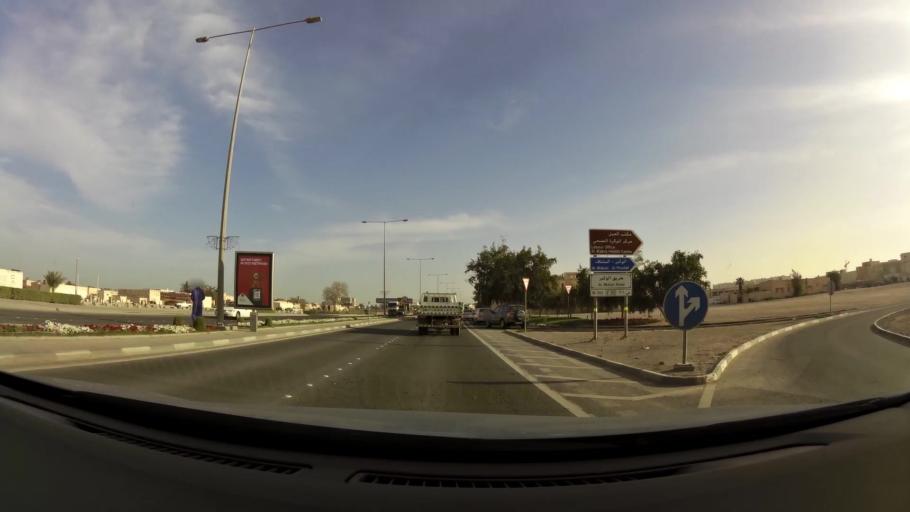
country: QA
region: Al Wakrah
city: Al Wakrah
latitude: 25.1717
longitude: 51.6072
